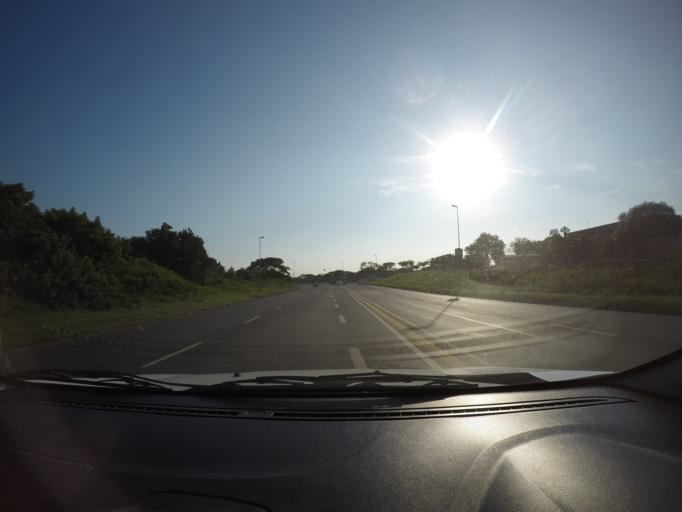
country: ZA
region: KwaZulu-Natal
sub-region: uThungulu District Municipality
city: Richards Bay
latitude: -28.7672
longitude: 32.0162
